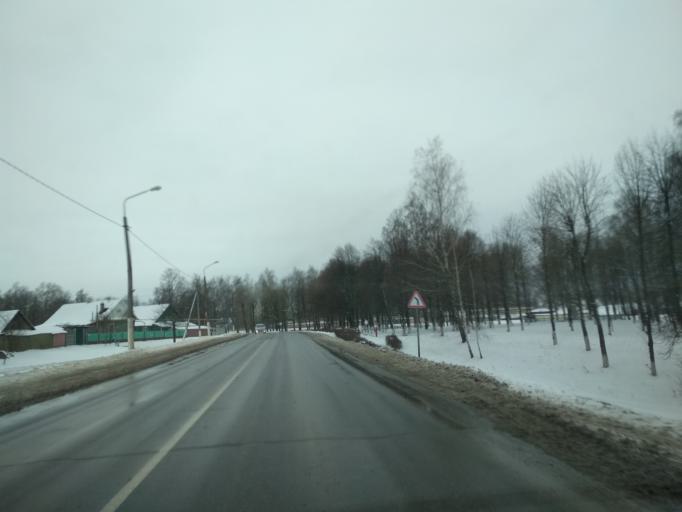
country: BY
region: Minsk
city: Mar''ina Horka
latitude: 53.5220
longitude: 28.1395
